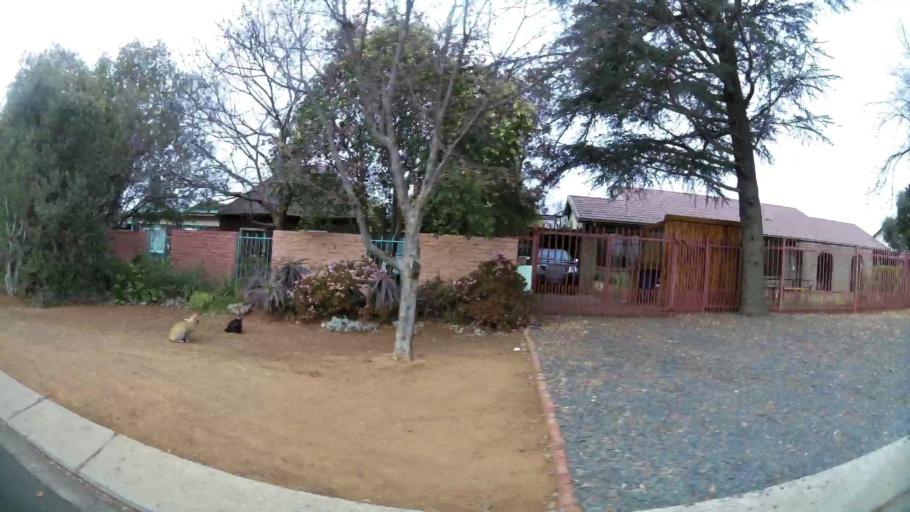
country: ZA
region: Orange Free State
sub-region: Mangaung Metropolitan Municipality
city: Bloemfontein
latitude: -29.1288
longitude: 26.1670
